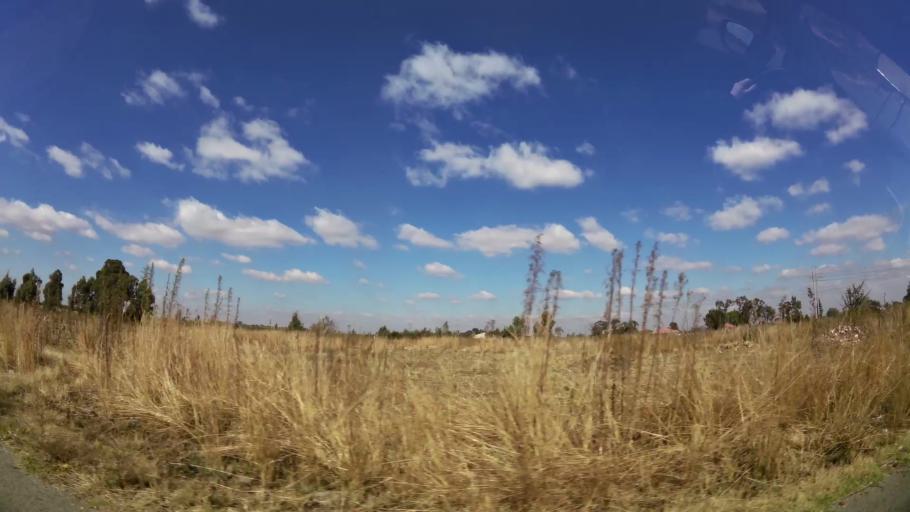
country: ZA
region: Gauteng
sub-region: West Rand District Municipality
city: Krugersdorp
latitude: -26.1249
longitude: 27.8054
